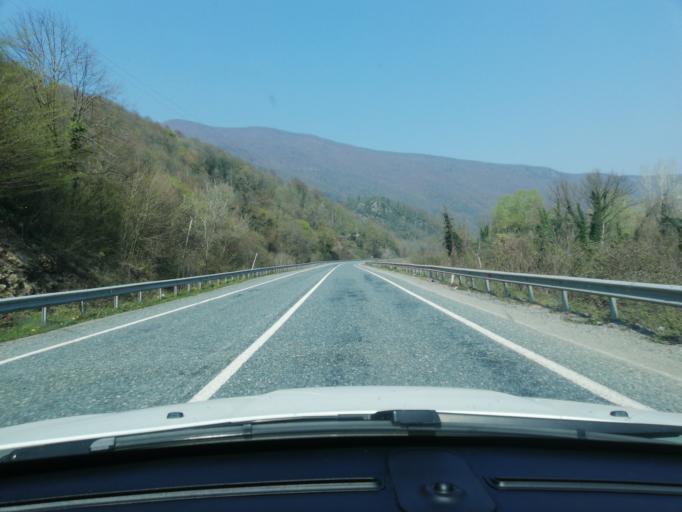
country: TR
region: Zonguldak
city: Gokcebey
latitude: 41.2565
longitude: 32.1593
